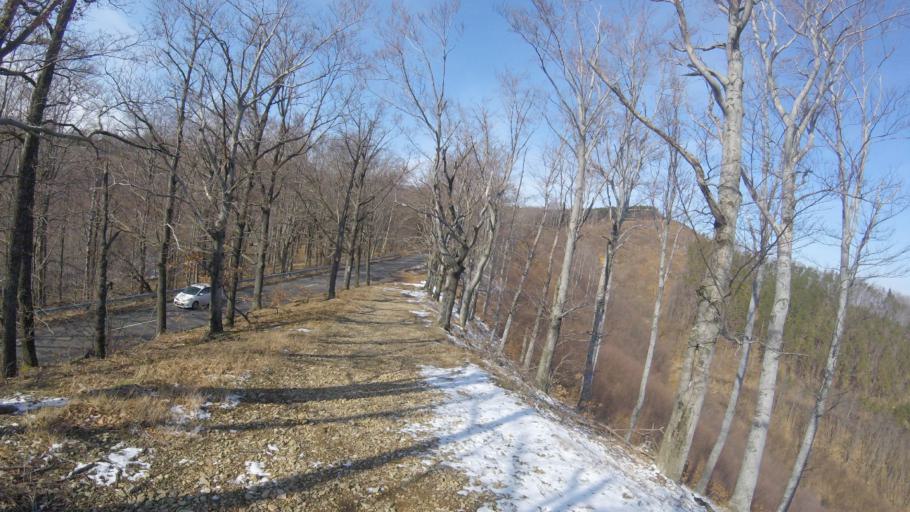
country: HU
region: Heves
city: Paradsasvar
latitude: 47.9068
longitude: 19.9507
